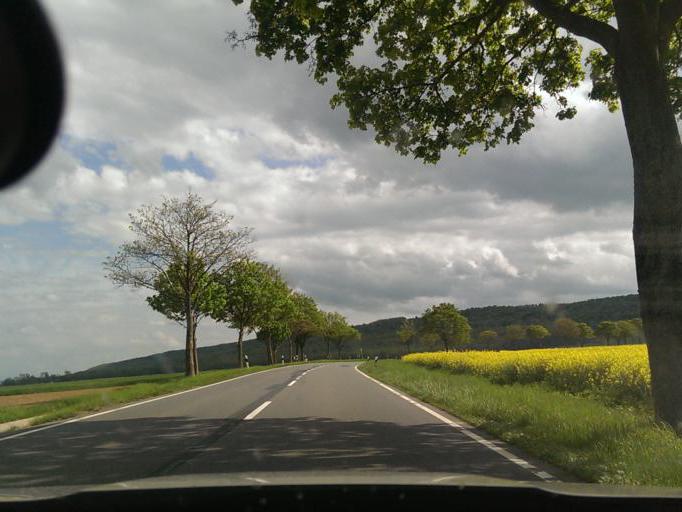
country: DE
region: Lower Saxony
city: Marienhagen
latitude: 52.0445
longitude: 9.6933
